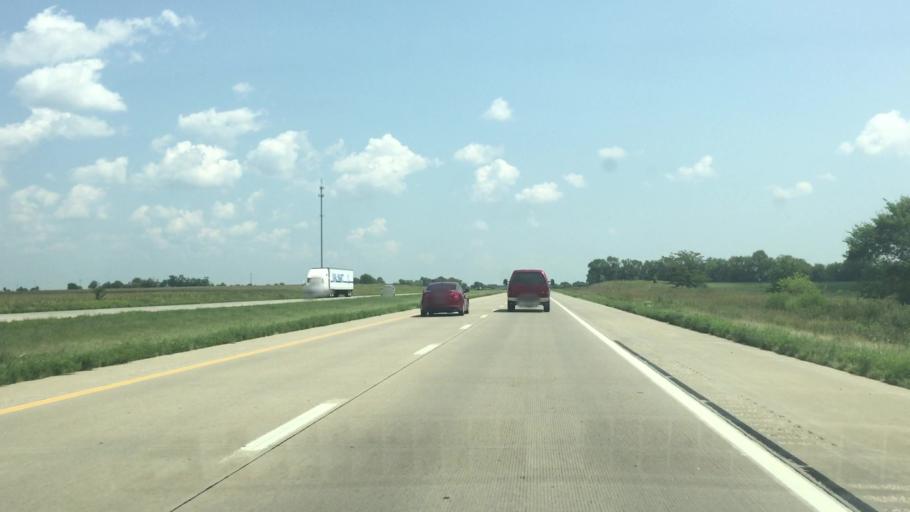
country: US
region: Kansas
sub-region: Franklin County
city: Wellsville
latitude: 38.6875
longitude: -95.1165
